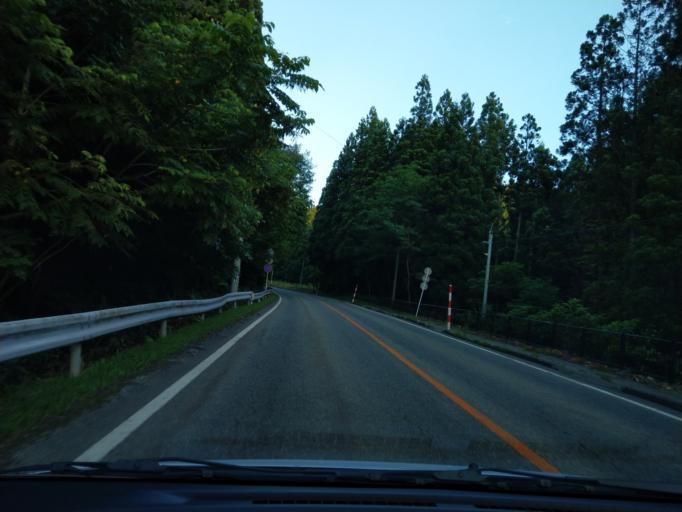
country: JP
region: Akita
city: Kakunodatemachi
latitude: 39.6036
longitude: 140.5709
